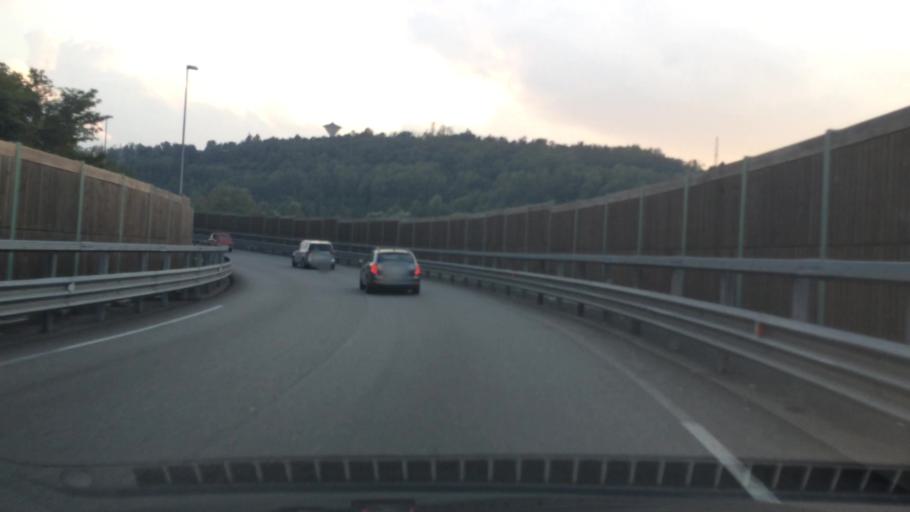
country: IT
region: Lombardy
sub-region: Provincia di Como
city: Casnate Con Bernate
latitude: 45.7777
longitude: 9.0749
